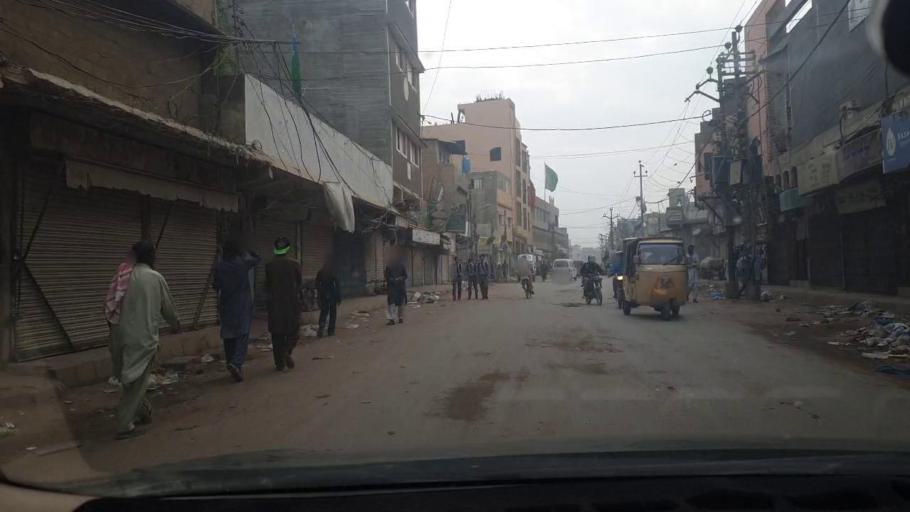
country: PK
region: Sindh
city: Malir Cantonment
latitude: 24.8787
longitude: 67.1902
